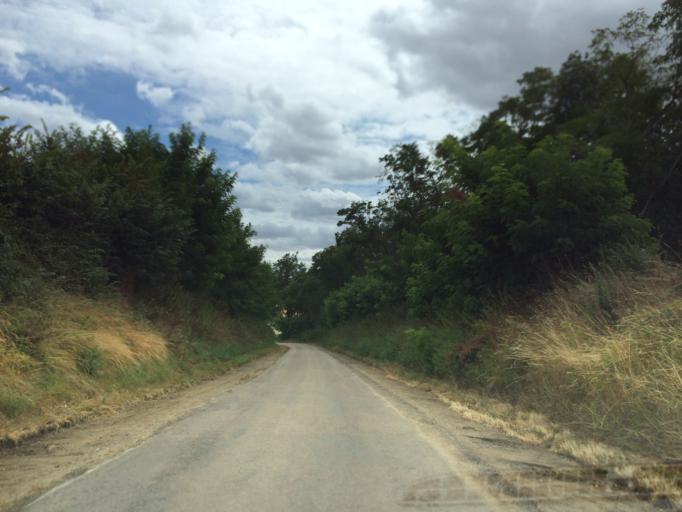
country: FR
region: Bourgogne
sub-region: Departement de l'Yonne
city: Fleury-la-Vallee
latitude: 47.8499
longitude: 3.4044
